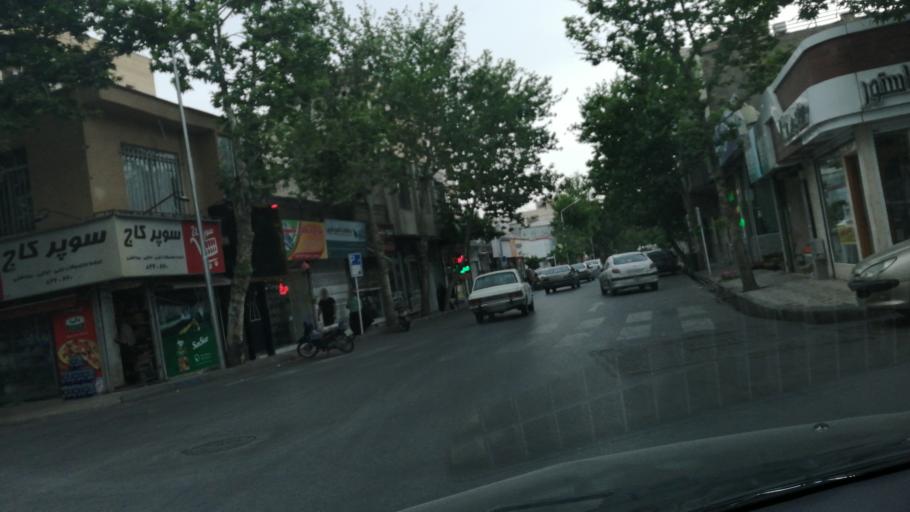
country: IR
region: Razavi Khorasan
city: Mashhad
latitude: 36.2969
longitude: 59.5824
